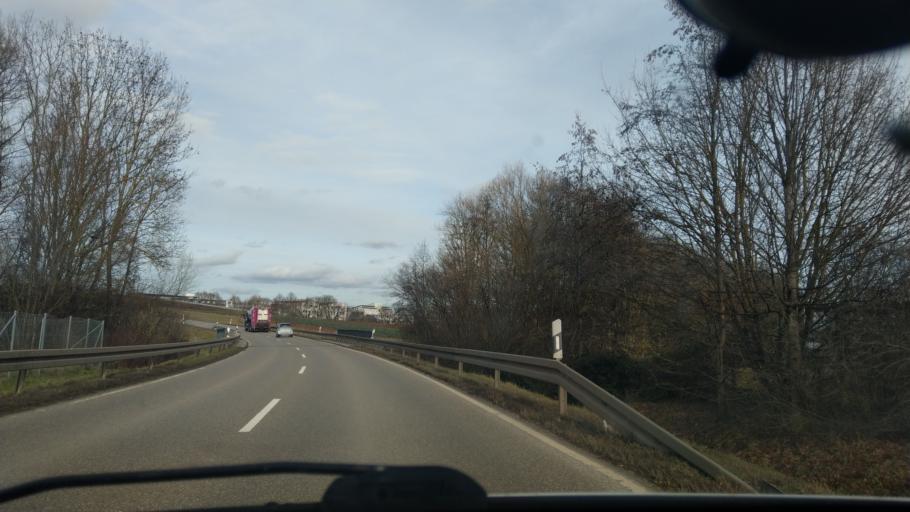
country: DE
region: Baden-Wuerttemberg
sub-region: Regierungsbezirk Stuttgart
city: Neuhausen auf den Fildern
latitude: 48.6860
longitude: 9.2619
